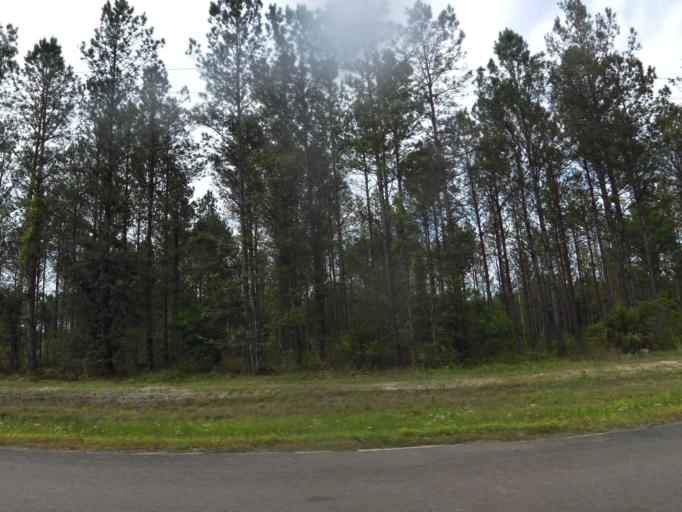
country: US
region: Georgia
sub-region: Camden County
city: Kingsland
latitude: 30.6987
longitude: -81.7762
